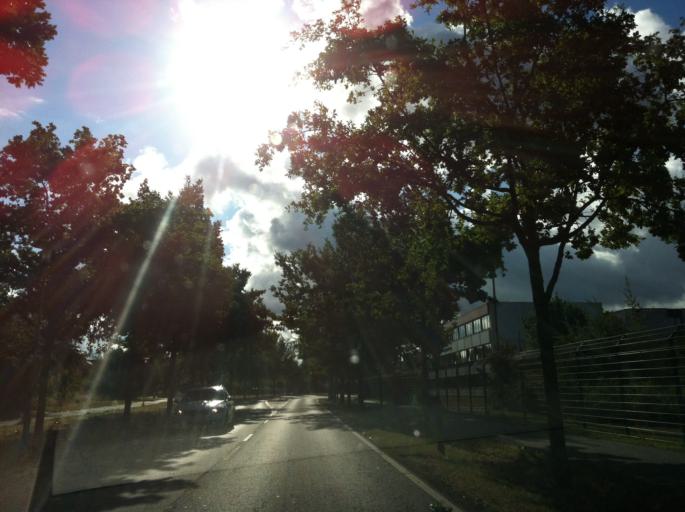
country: DE
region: Hesse
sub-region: Regierungsbezirk Darmstadt
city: Darmstadt
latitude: 49.9016
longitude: 8.6514
